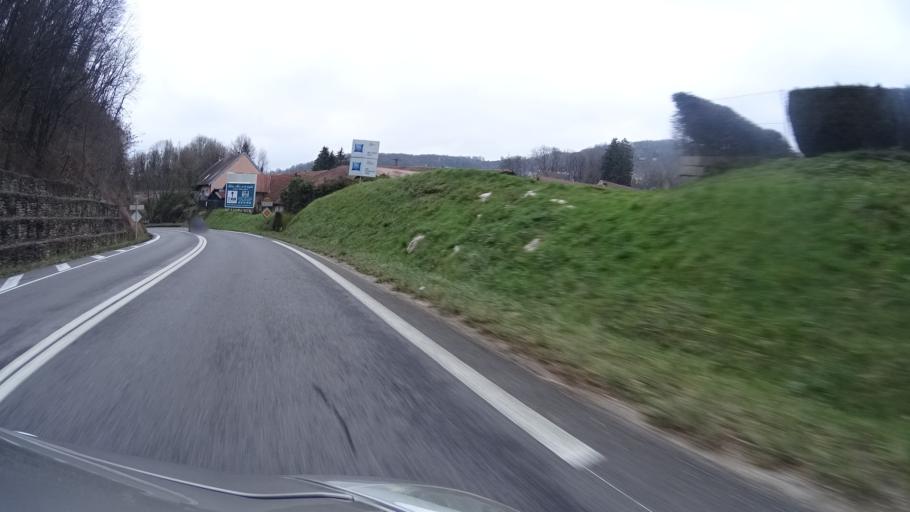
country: FR
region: Franche-Comte
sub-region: Departement du Doubs
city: Morre
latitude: 47.2255
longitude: 6.0642
